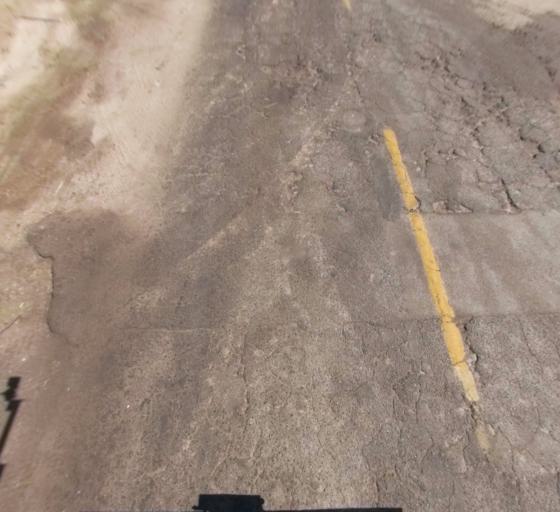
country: US
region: California
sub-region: Fresno County
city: Biola
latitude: 36.8586
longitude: -120.0374
